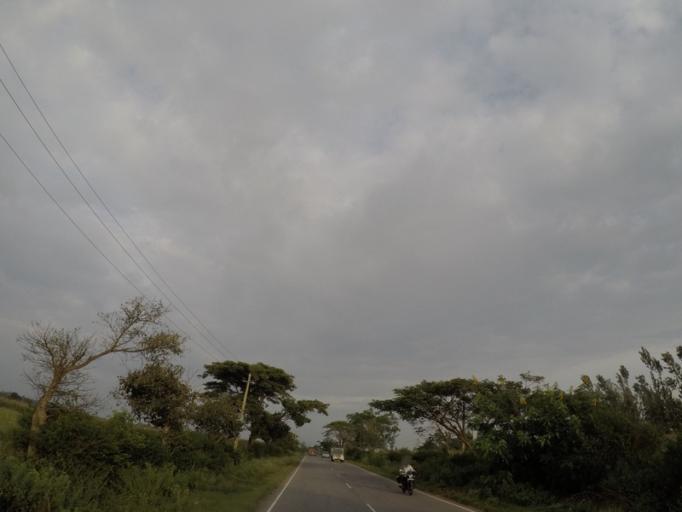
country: IN
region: Karnataka
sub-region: Hassan
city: Belur
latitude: 13.2218
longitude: 75.8677
